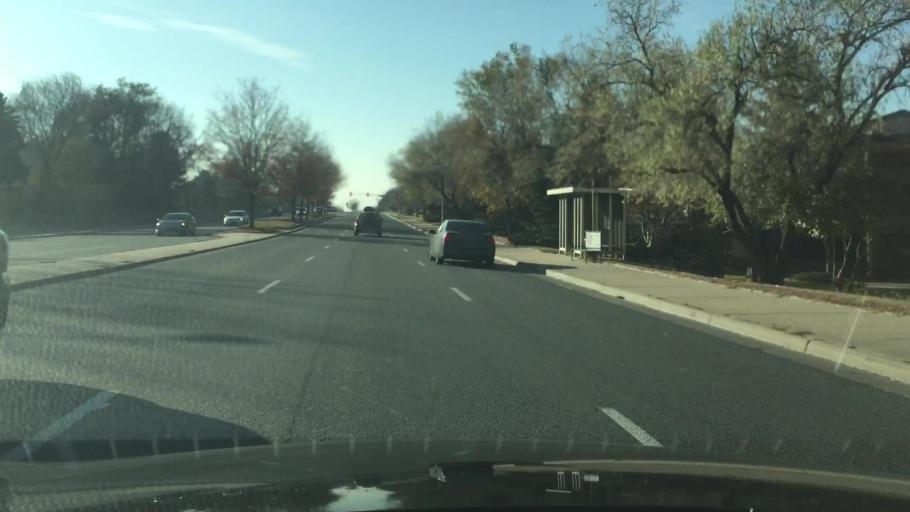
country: US
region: Colorado
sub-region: Arapahoe County
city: Dove Valley
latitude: 39.6532
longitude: -104.8170
